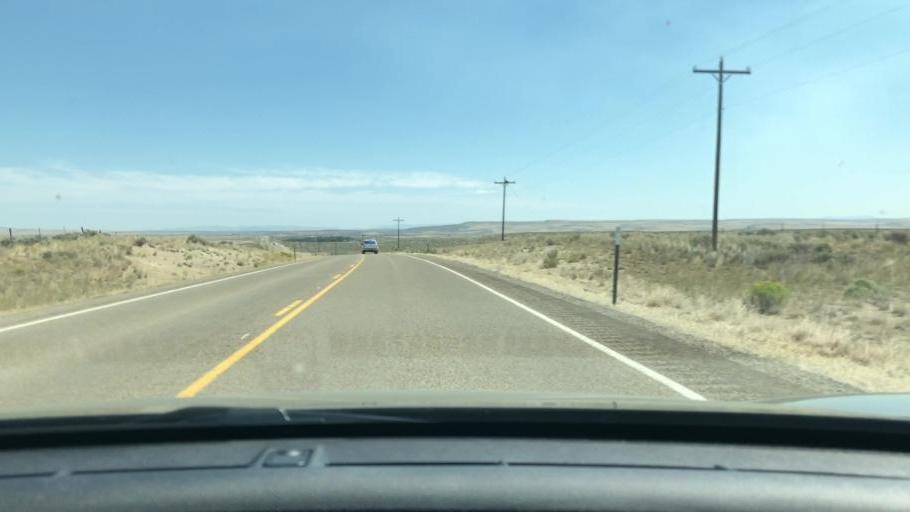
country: US
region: Idaho
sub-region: Owyhee County
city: Homedale
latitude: 42.8595
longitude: -117.5578
